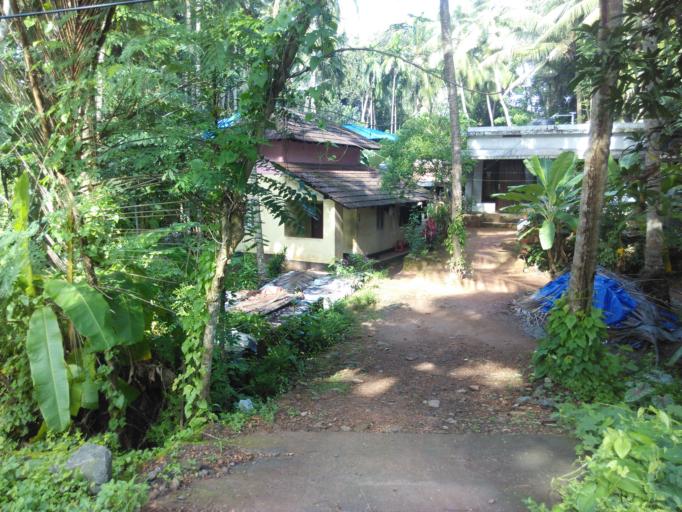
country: IN
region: Kerala
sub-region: Kozhikode
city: Kozhikode
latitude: 11.2819
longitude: 75.8063
